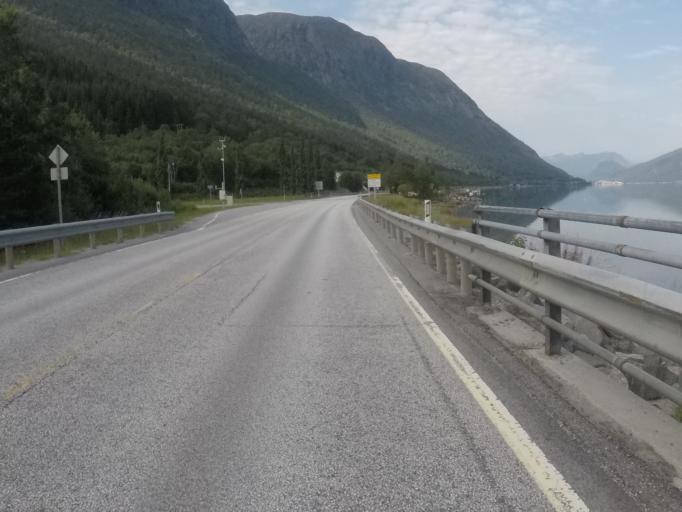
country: NO
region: More og Romsdal
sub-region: Rauma
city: Andalsnes
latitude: 62.5716
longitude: 7.7847
